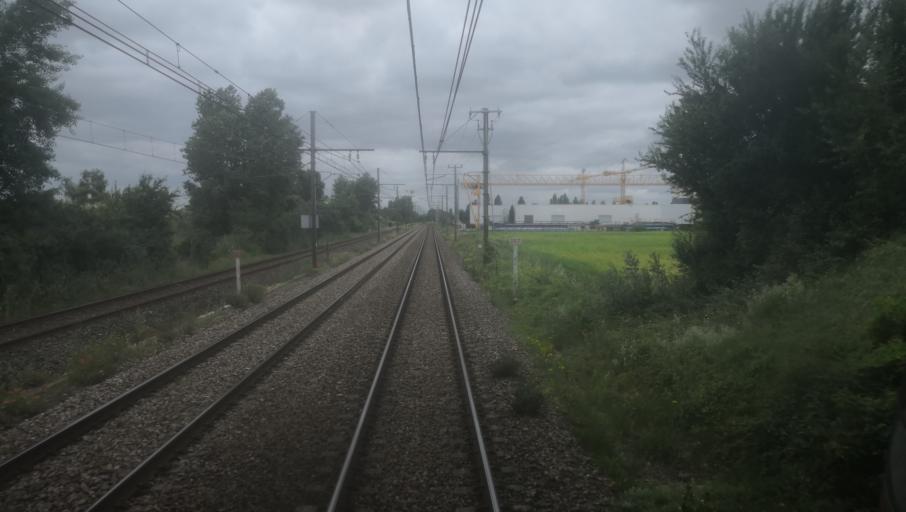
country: FR
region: Midi-Pyrenees
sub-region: Departement de la Haute-Garonne
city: Labege
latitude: 43.5353
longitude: 1.5263
